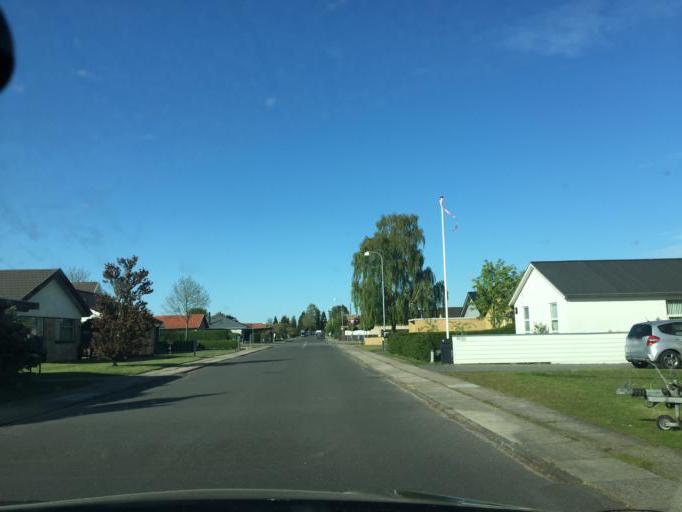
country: DK
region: South Denmark
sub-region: Odense Kommune
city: Bellinge
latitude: 55.3558
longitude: 10.3431
